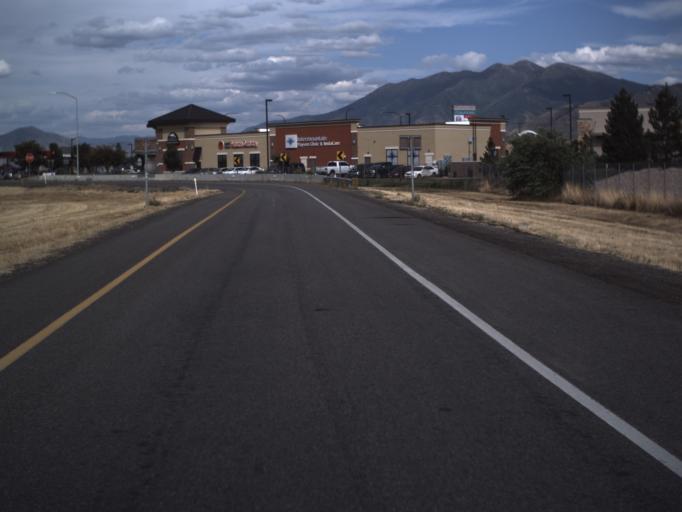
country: US
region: Utah
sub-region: Utah County
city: Payson
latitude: 40.0301
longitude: -111.7572
